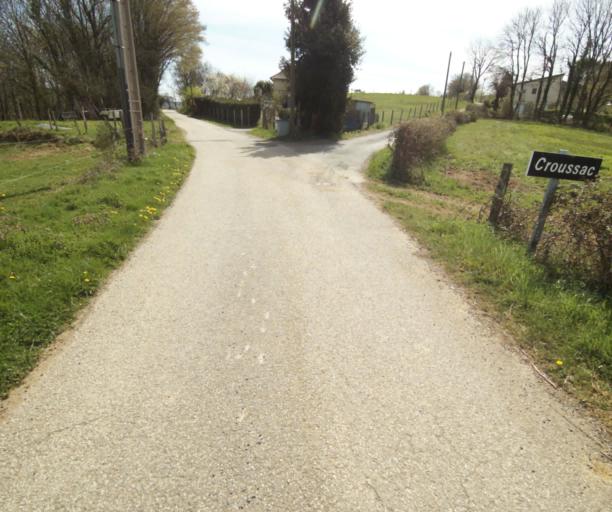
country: FR
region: Limousin
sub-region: Departement de la Correze
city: Naves
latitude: 45.3534
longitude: 1.7971
